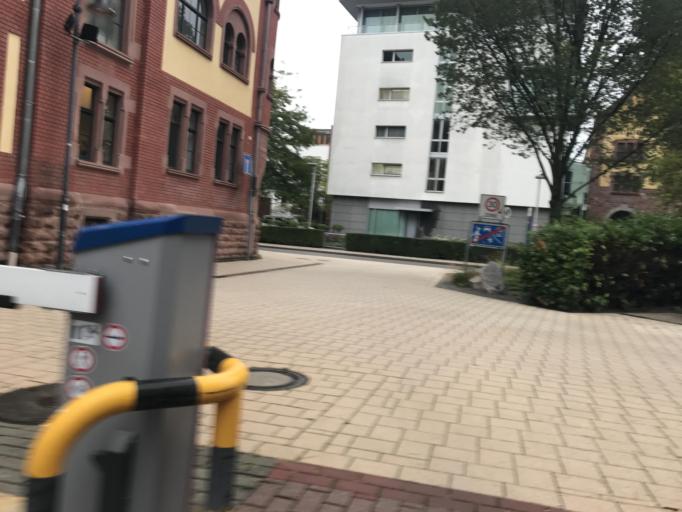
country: DE
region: Baden-Wuerttemberg
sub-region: Karlsruhe Region
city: Heidelberg
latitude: 49.4063
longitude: 8.6829
